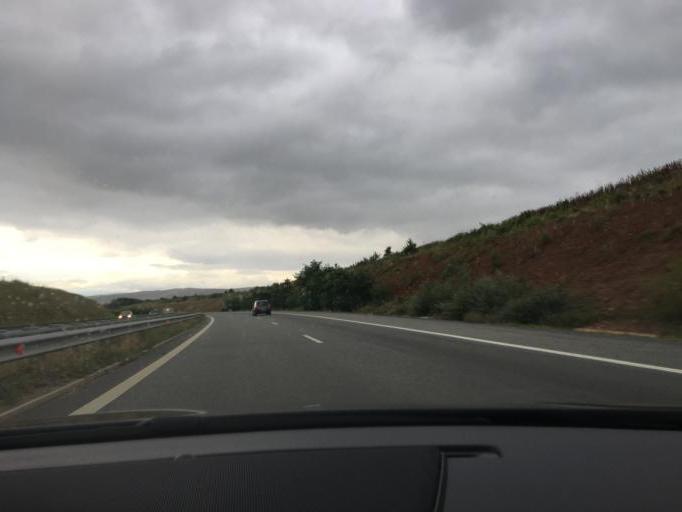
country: BG
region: Kyustendil
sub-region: Obshtina Bobovdol
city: Bobovdol
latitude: 42.3676
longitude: 23.1066
